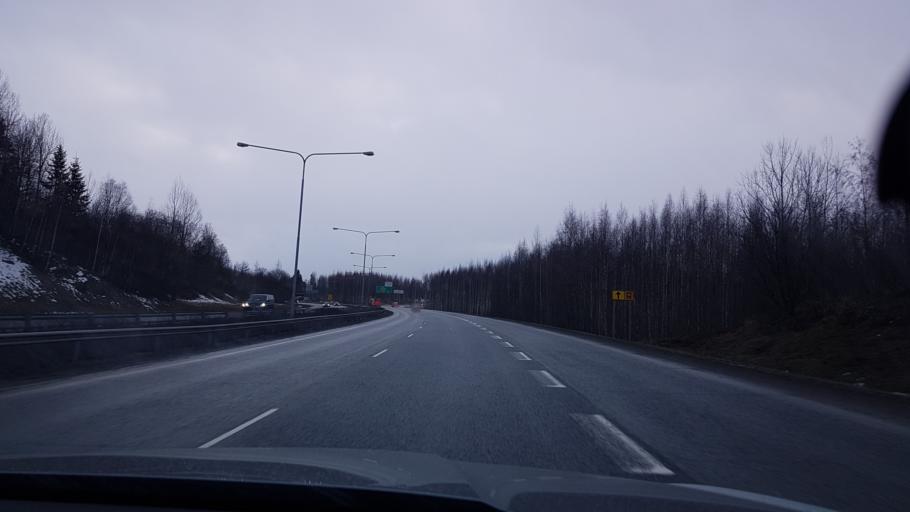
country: FI
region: Pirkanmaa
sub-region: Tampere
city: Tampere
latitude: 61.4943
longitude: 23.8771
